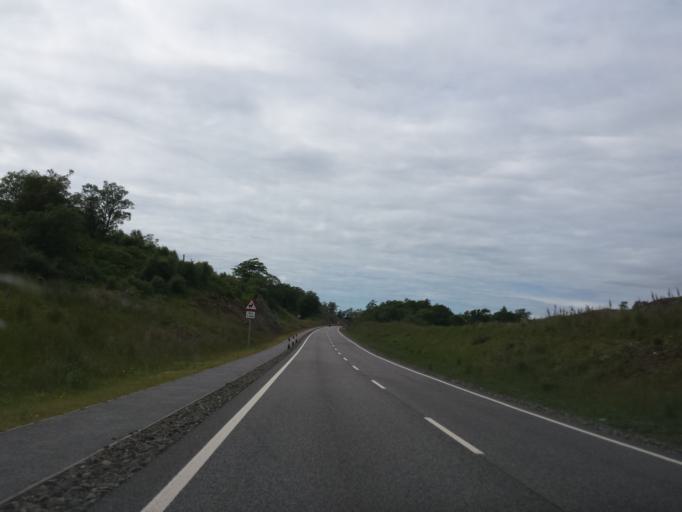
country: GB
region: Scotland
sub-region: Argyll and Bute
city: Isle Of Mull
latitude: 56.9032
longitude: -5.8114
